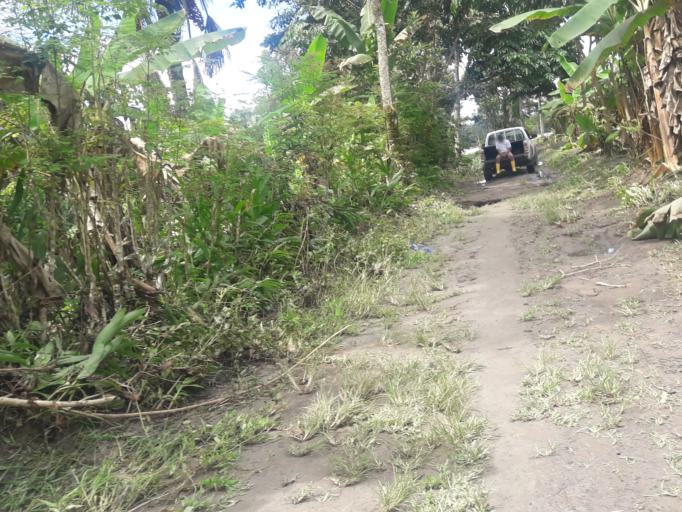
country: EC
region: Napo
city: Tena
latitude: -1.0416
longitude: -77.7864
